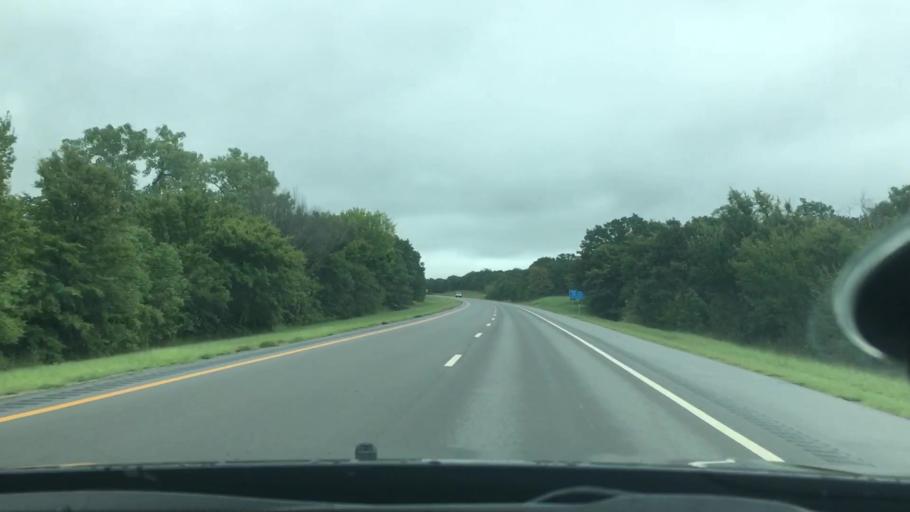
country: US
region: Oklahoma
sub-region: Okmulgee County
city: Morris
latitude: 35.4338
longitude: -95.7971
